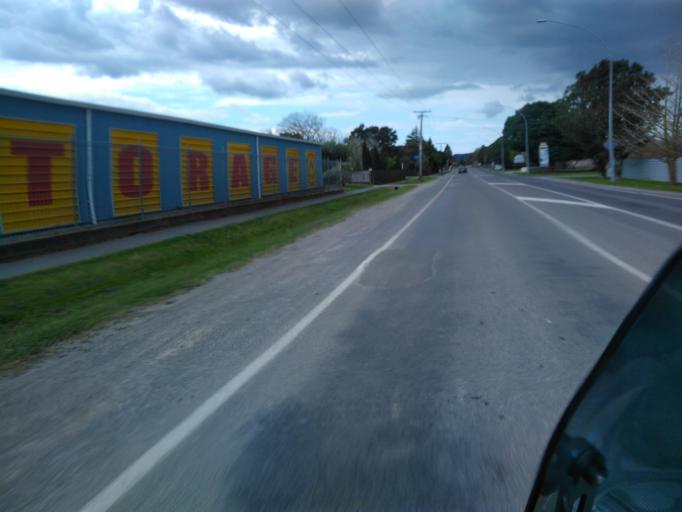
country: NZ
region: Gisborne
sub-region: Gisborne District
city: Gisborne
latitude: -38.6490
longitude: 177.9727
